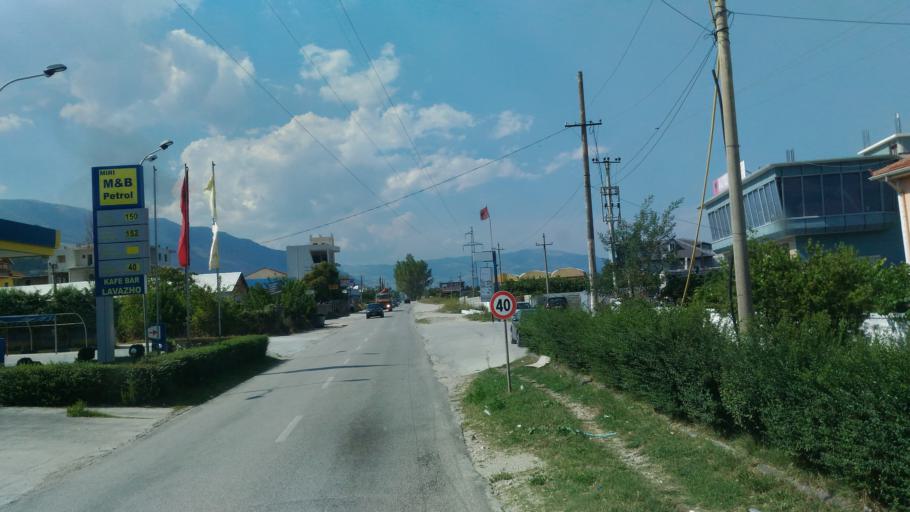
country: AL
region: Gjirokaster
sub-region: Rrethi i Gjirokastres
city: Lazarat
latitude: 40.0665
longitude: 20.1641
